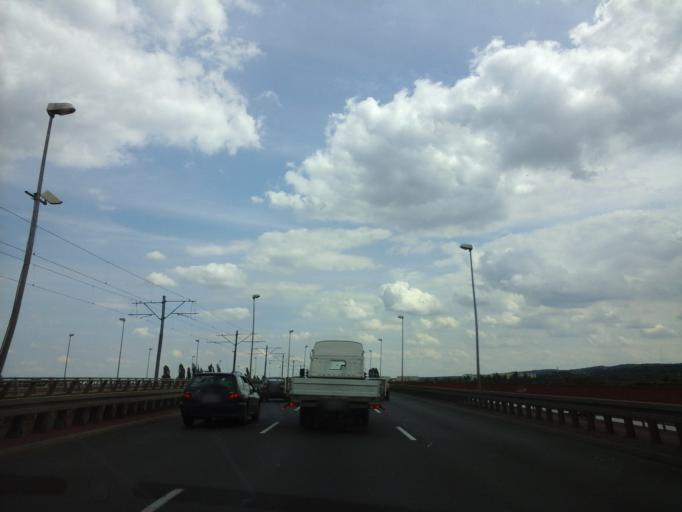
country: PL
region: West Pomeranian Voivodeship
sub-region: Szczecin
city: Szczecin
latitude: 53.3942
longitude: 14.6114
